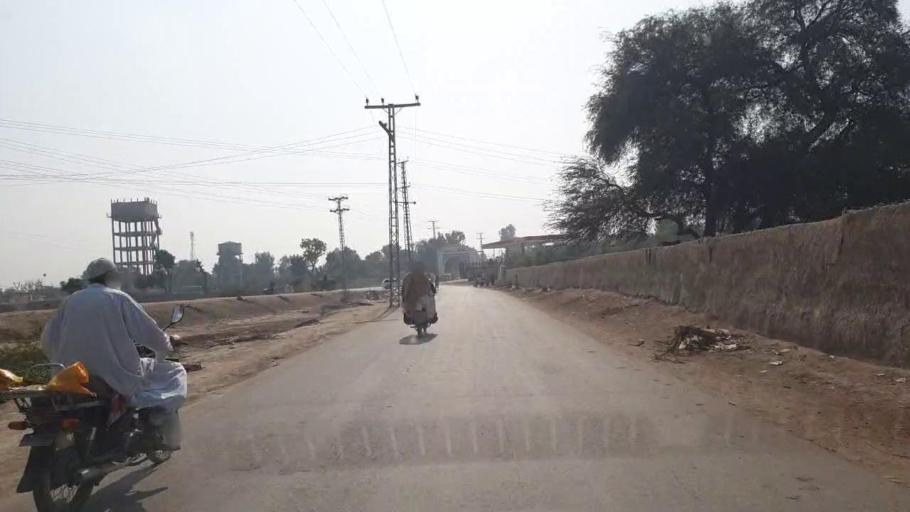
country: PK
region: Sindh
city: Hala
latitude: 25.8212
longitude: 68.4189
